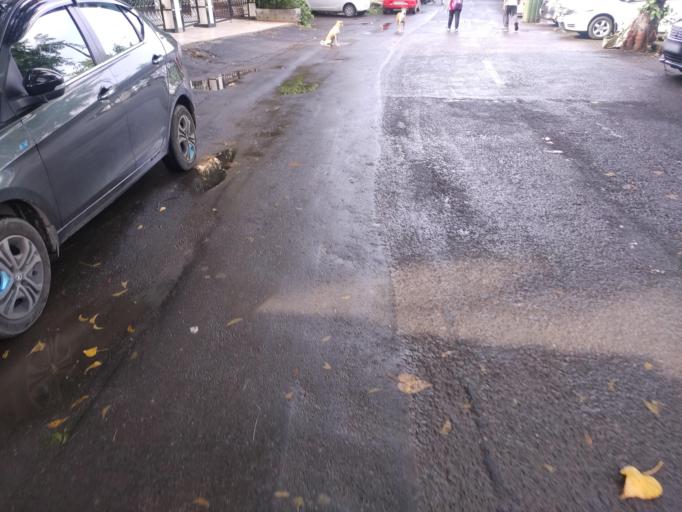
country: IN
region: Maharashtra
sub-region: Mumbai Suburban
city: Borivli
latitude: 19.2459
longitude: 72.8574
